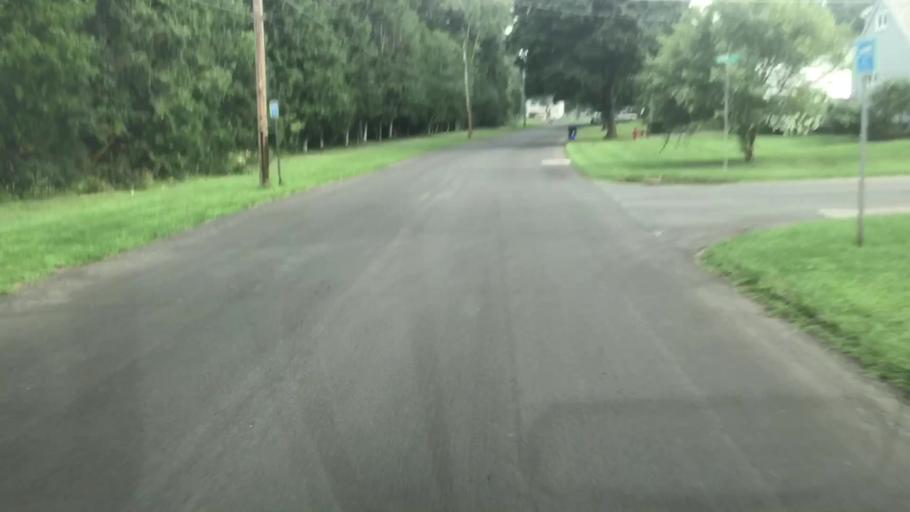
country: US
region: New York
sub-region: Onondaga County
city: Liverpool
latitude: 43.1382
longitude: -76.2241
